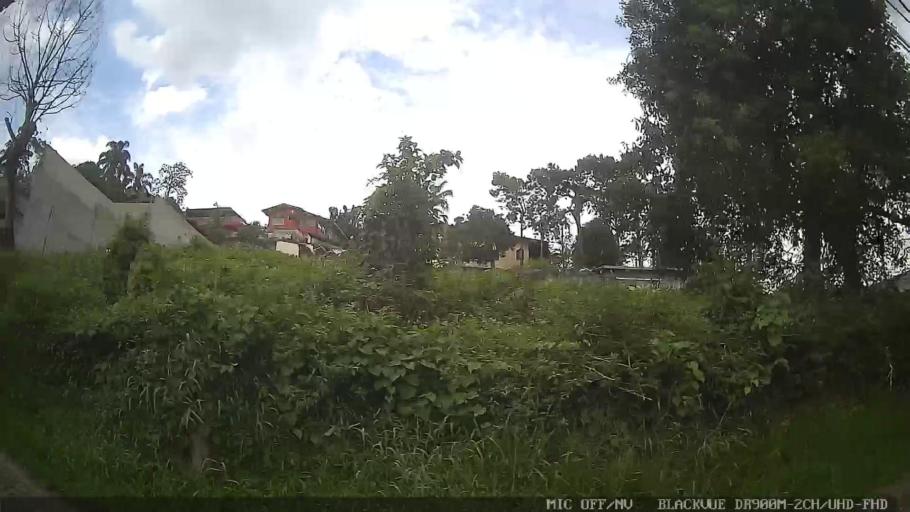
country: BR
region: Sao Paulo
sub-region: Ribeirao Pires
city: Ribeirao Pires
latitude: -23.6966
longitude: -46.3959
